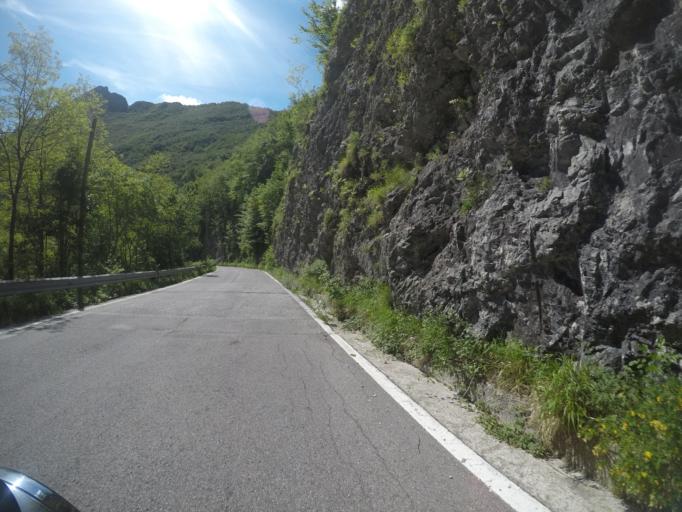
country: IT
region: Tuscany
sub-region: Provincia di Lucca
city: Fontana delle Monache
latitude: 44.0575
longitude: 10.2645
